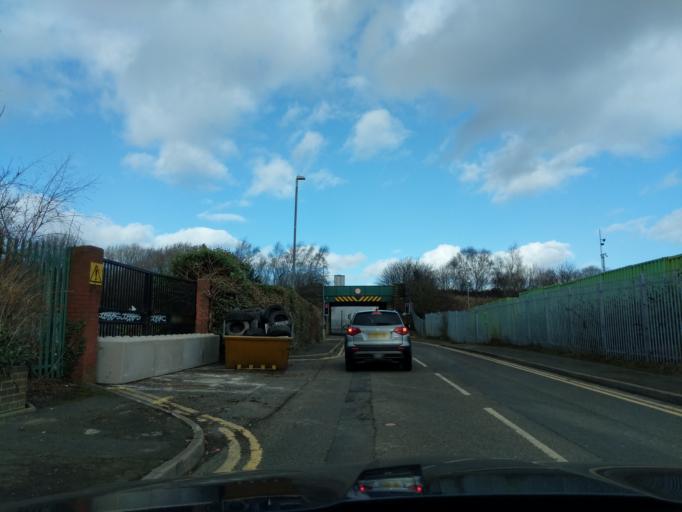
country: GB
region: England
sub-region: Newcastle upon Tyne
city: Benwell
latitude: 54.9577
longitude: -1.6599
